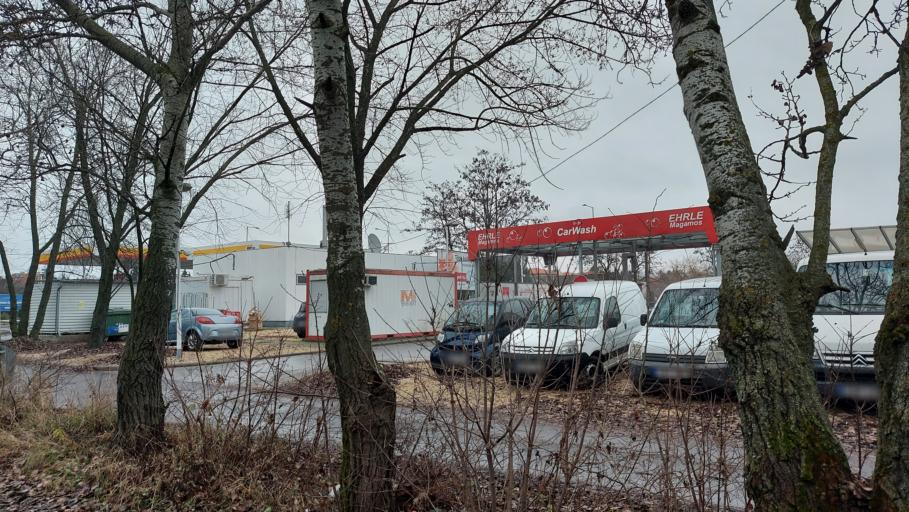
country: HU
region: Budapest
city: Budapest XXII. keruelet
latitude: 47.4353
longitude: 19.0058
